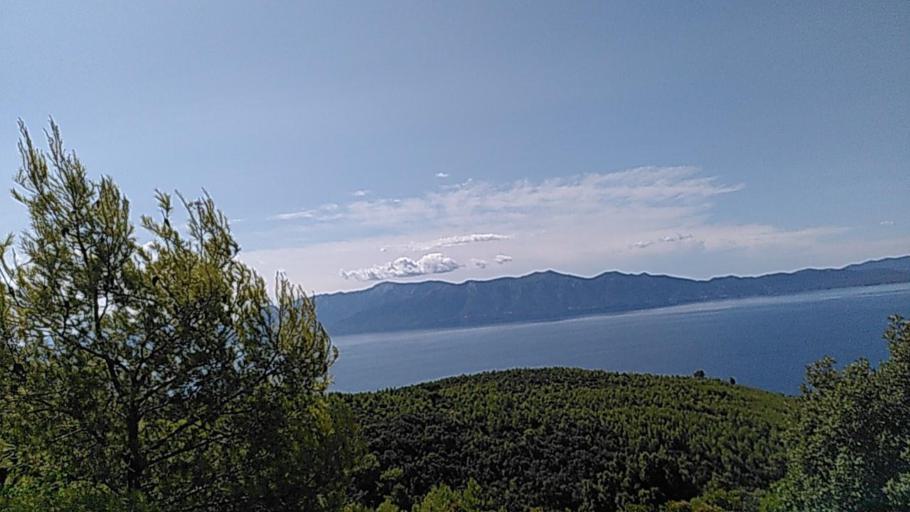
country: HR
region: Dubrovacko-Neretvanska
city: Orebic
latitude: 43.1225
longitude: 17.1134
